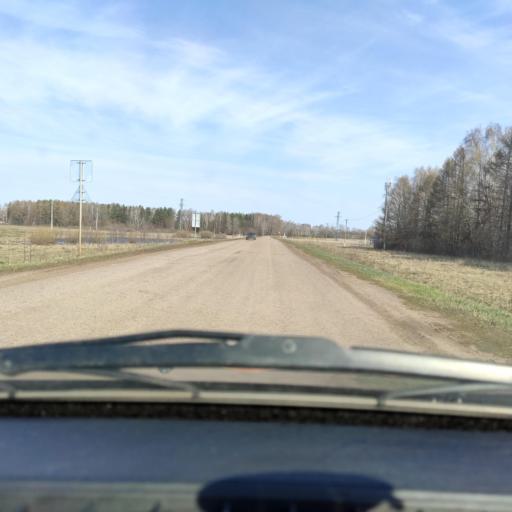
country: RU
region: Bashkortostan
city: Asanovo
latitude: 54.7685
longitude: 55.4874
